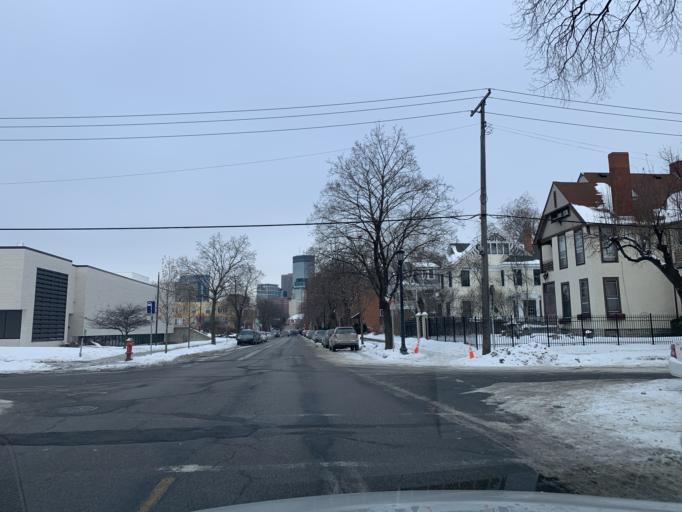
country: US
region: Minnesota
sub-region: Hennepin County
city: Minneapolis
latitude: 44.9608
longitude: -93.2727
